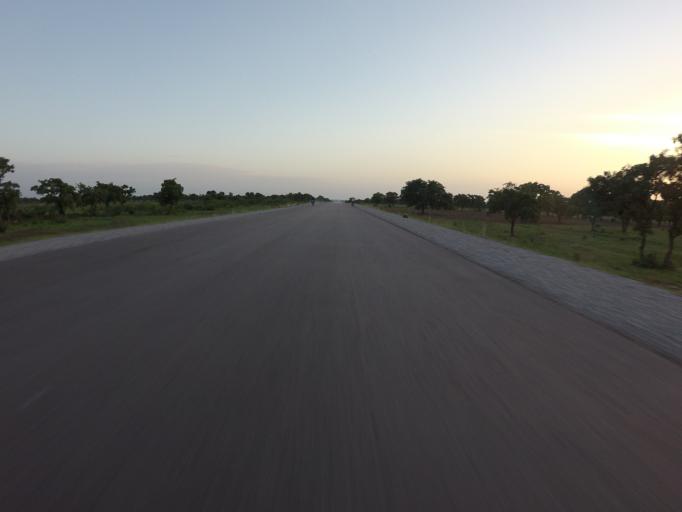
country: GH
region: Northern
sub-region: Yendi
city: Yendi
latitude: 9.9478
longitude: -0.1587
